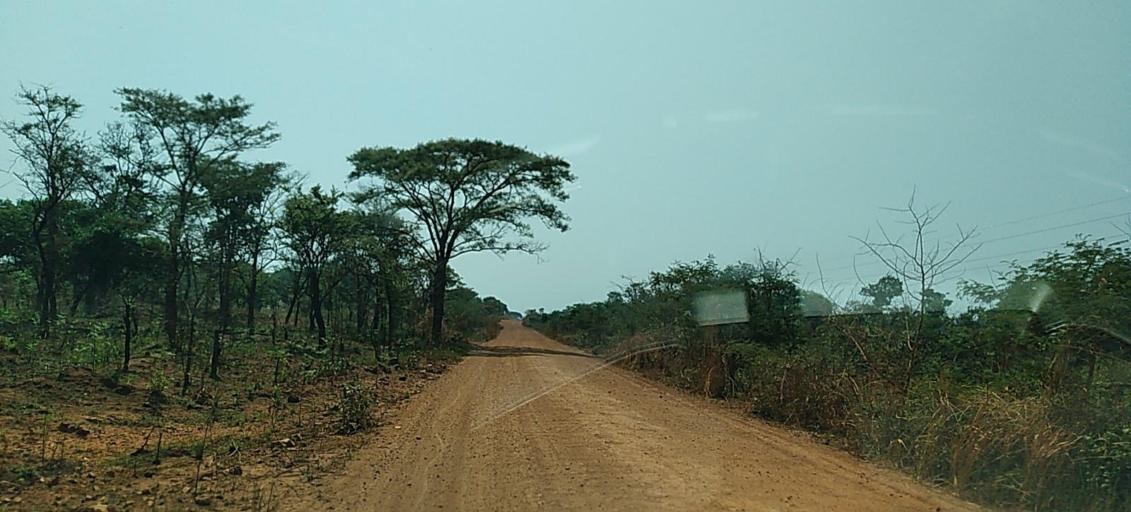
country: ZM
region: North-Western
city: Kansanshi
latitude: -12.0055
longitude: 26.5385
